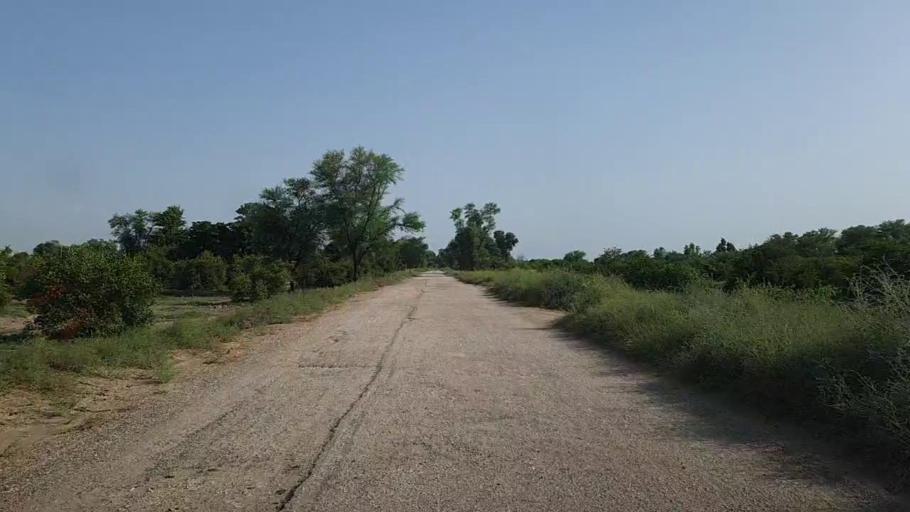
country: PK
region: Sindh
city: Karaundi
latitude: 26.8599
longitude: 68.3309
